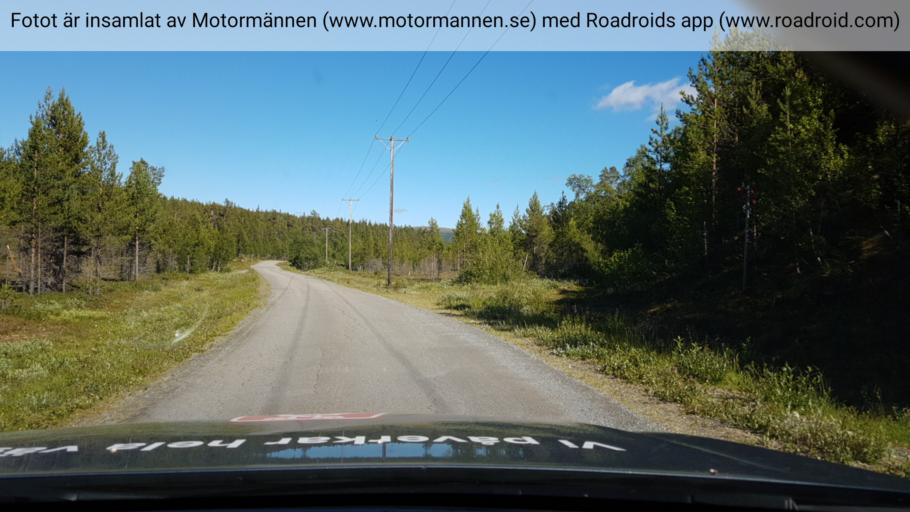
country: SE
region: Jaemtland
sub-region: Are Kommun
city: Are
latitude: 63.1491
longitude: 12.9319
